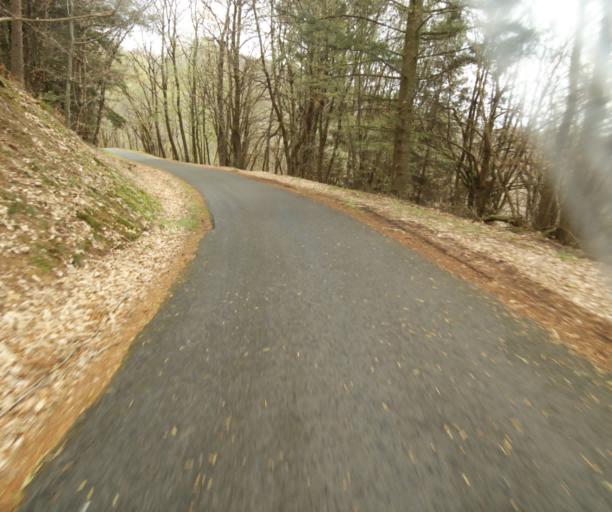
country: FR
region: Limousin
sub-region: Departement de la Correze
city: Naves
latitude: 45.3037
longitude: 1.8099
